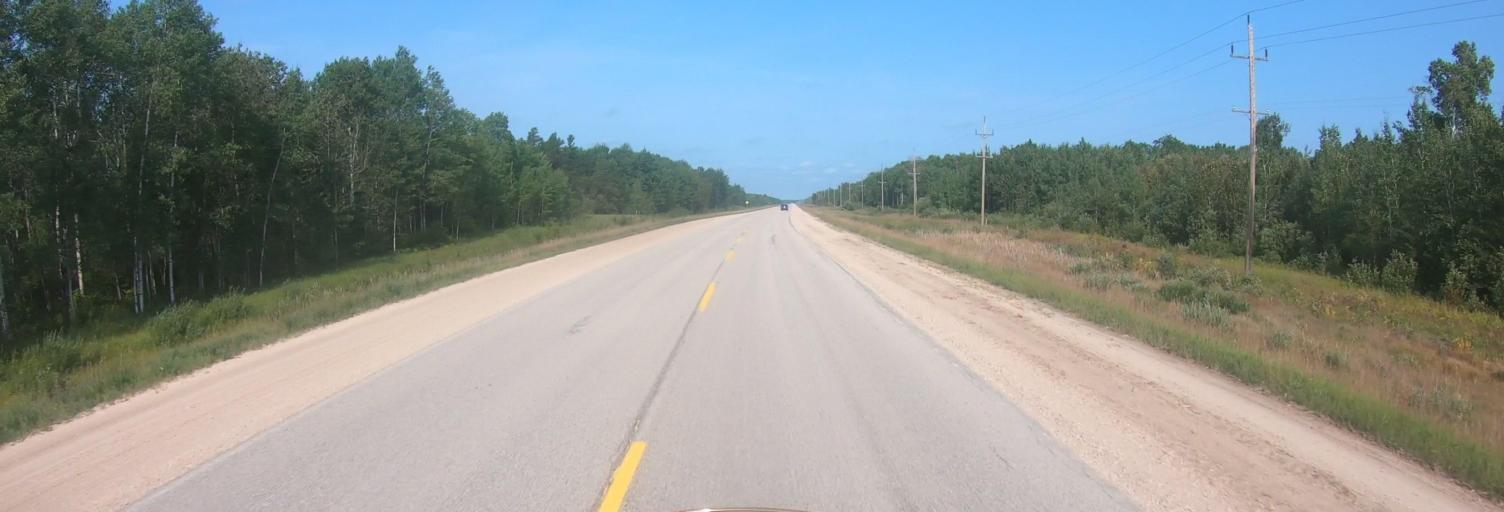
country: US
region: Minnesota
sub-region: Roseau County
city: Roseau
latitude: 49.1404
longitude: -96.1045
